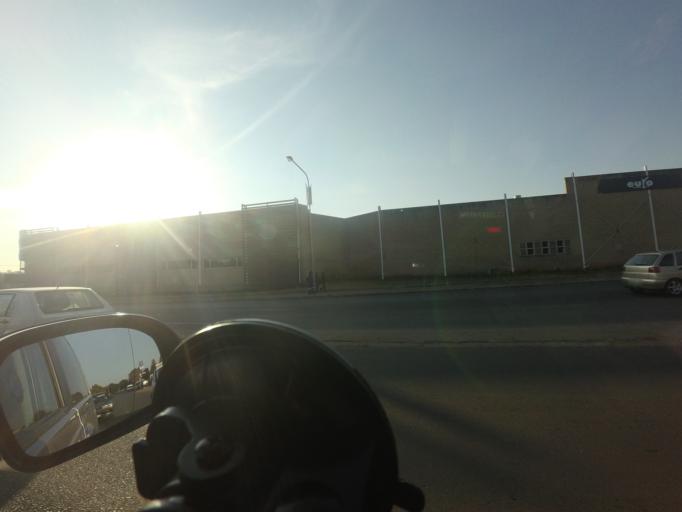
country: ZA
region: Gauteng
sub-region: Sedibeng District Municipality
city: Vereeniging
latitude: -26.6577
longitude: 27.9609
